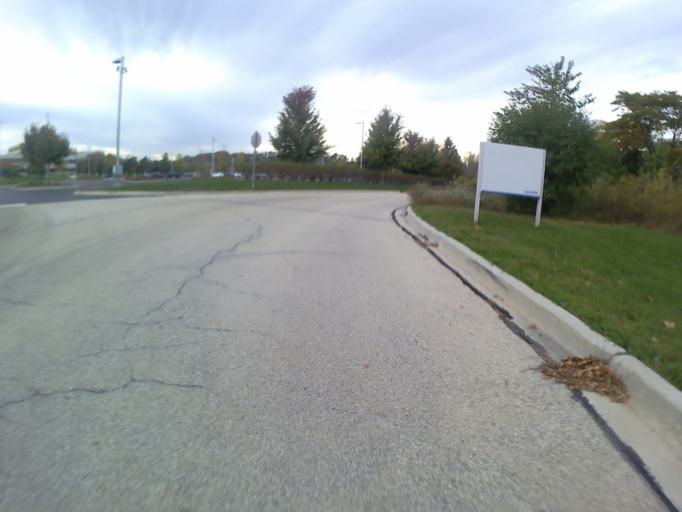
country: US
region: Illinois
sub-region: DuPage County
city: Lisle
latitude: 41.8120
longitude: -88.1037
